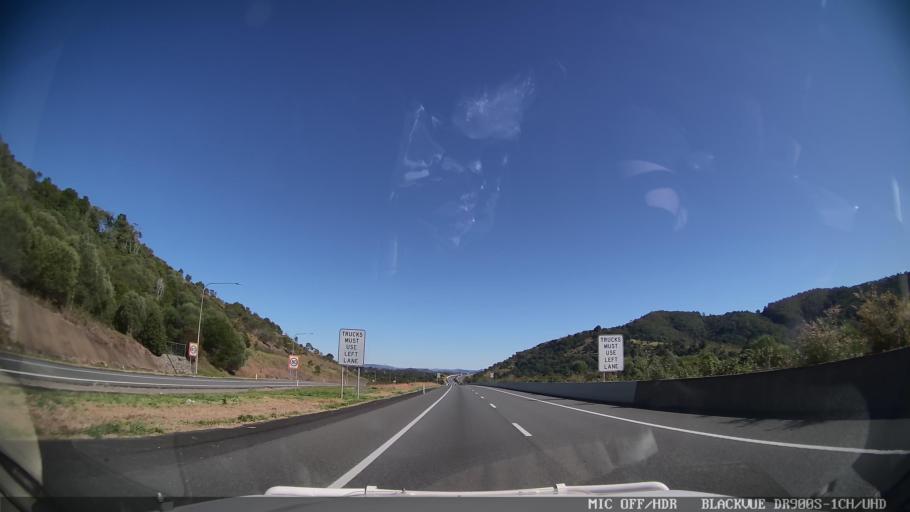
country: AU
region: Queensland
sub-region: Sunshine Coast
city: Black Mountain
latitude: -26.3888
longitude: 152.8011
